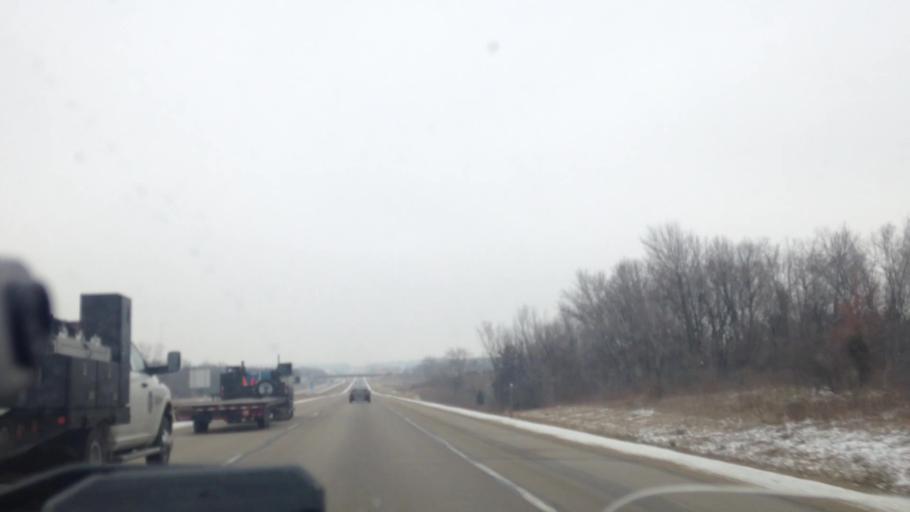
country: US
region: Wisconsin
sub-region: Washington County
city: Slinger
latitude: 43.3158
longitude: -88.2390
